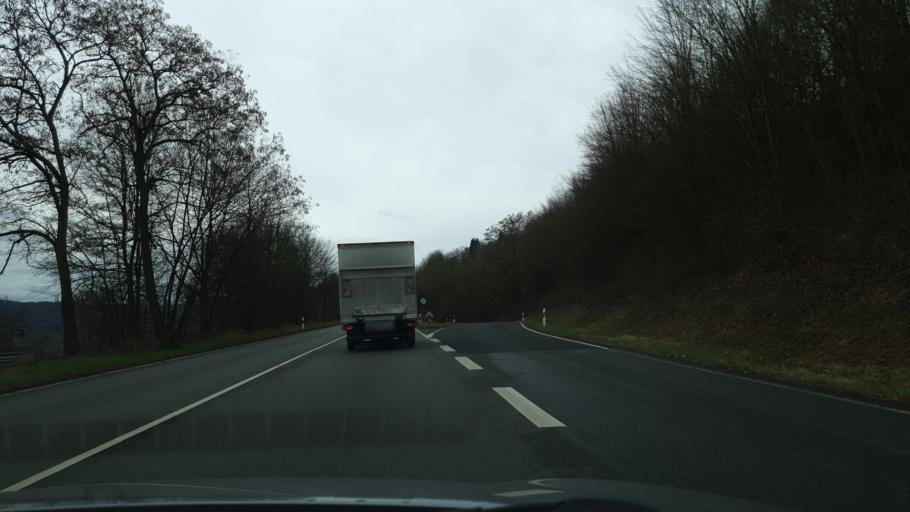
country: DE
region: Rheinland-Pfalz
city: Rhens
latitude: 50.2892
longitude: 7.6056
